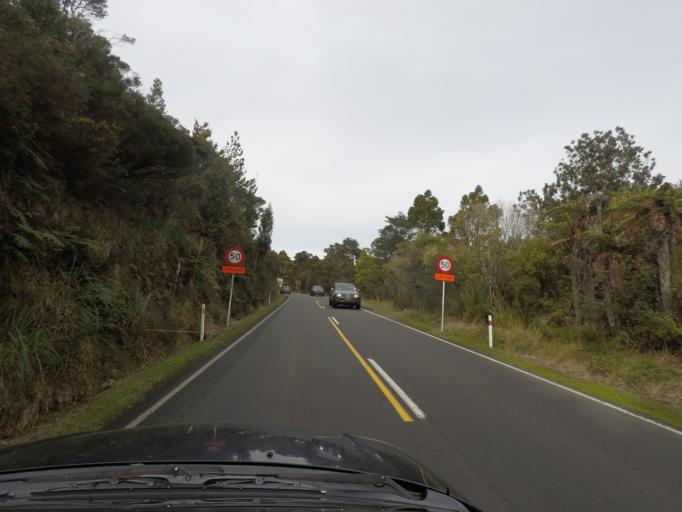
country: NZ
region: Auckland
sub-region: Auckland
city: Titirangi
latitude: -36.9330
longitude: 174.5717
